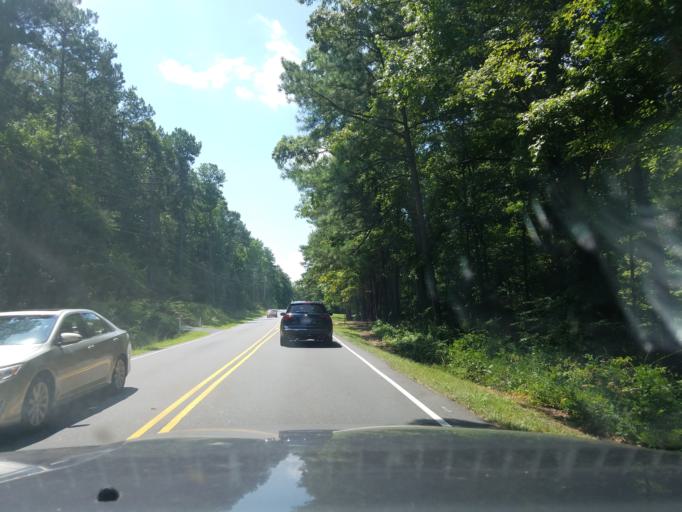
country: US
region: North Carolina
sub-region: Durham County
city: Durham
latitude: 35.9378
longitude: -78.9636
